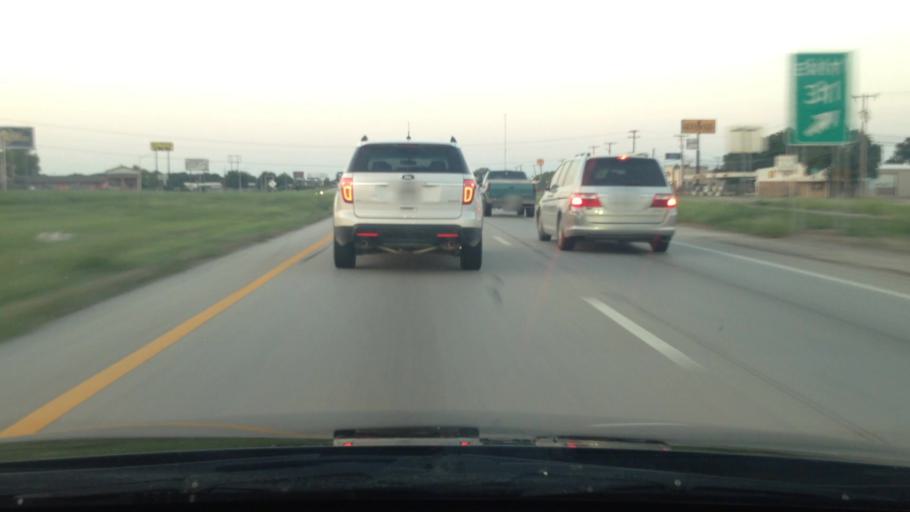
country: US
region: Texas
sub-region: Tarrant County
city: Forest Hill
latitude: 32.7043
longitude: -97.2334
